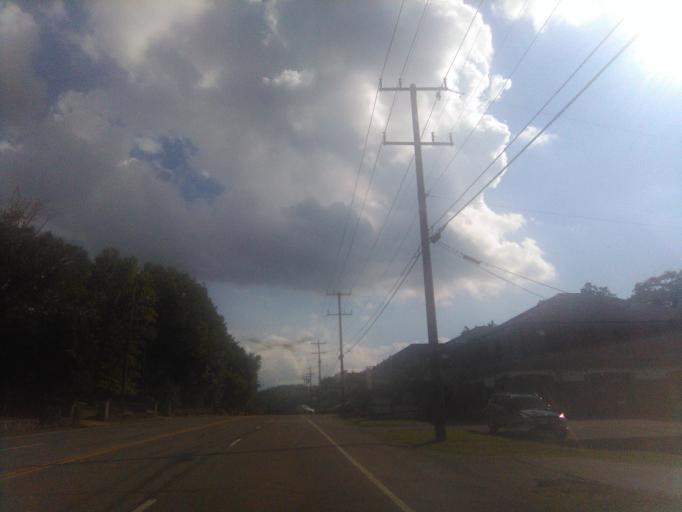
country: US
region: Tennessee
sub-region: Davidson County
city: Belle Meade
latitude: 36.0914
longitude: -86.8783
